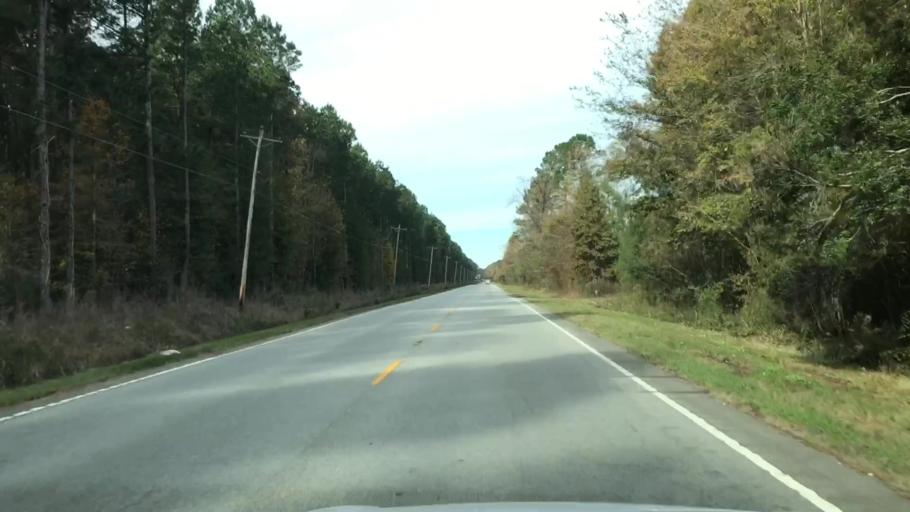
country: US
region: South Carolina
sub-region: Colleton County
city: Walterboro
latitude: 32.8159
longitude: -80.5392
